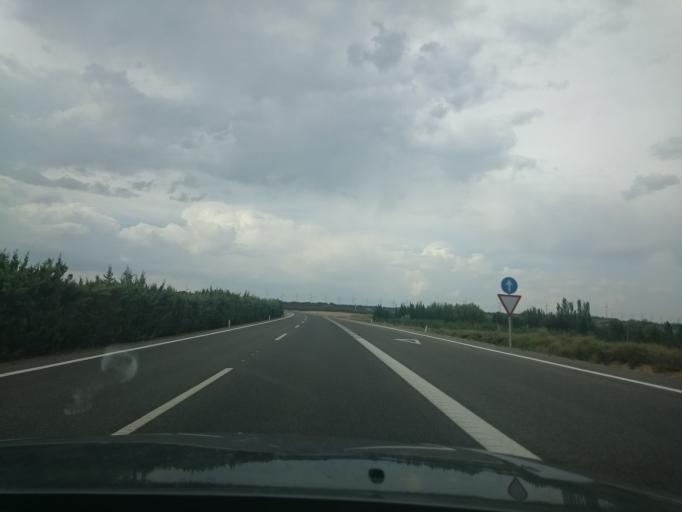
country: ES
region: Navarre
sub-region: Provincia de Navarra
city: Murchante
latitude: 42.0677
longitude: -1.6904
